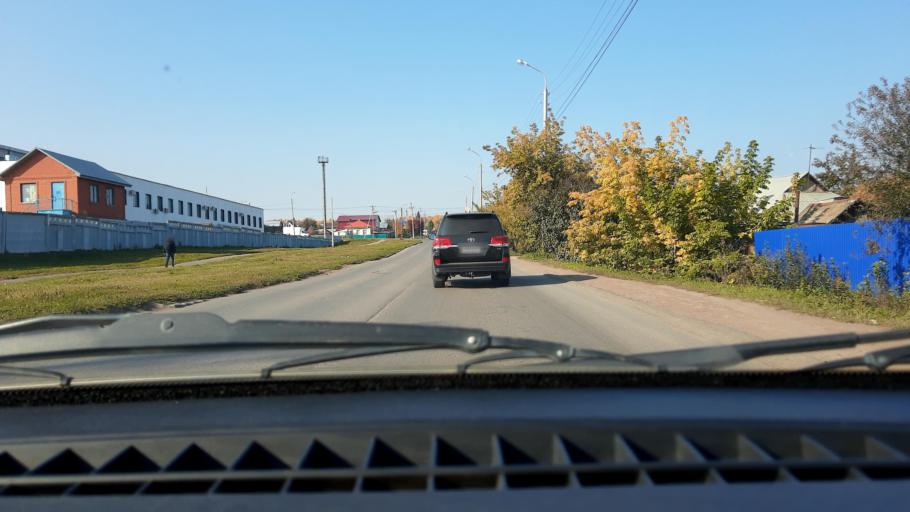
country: RU
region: Bashkortostan
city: Avdon
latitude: 54.6885
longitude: 55.8087
